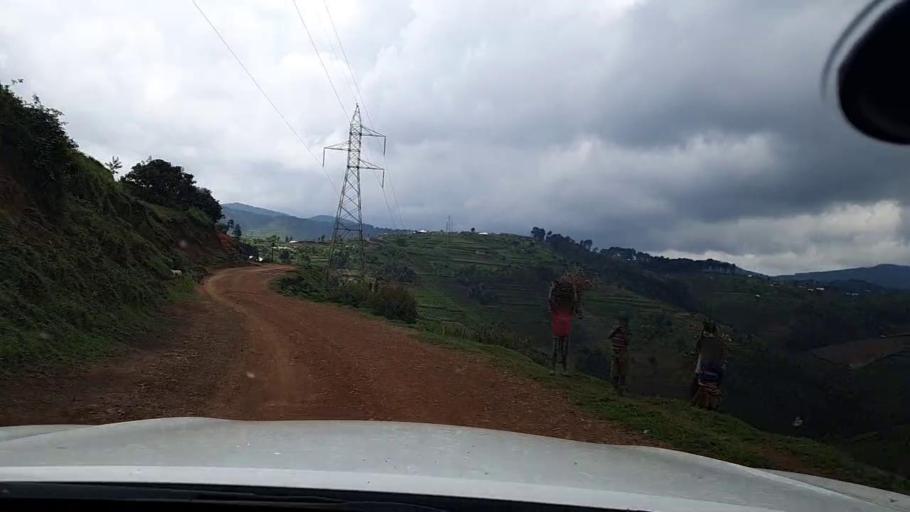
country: RW
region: Western Province
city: Kibuye
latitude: -2.1692
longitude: 29.4264
